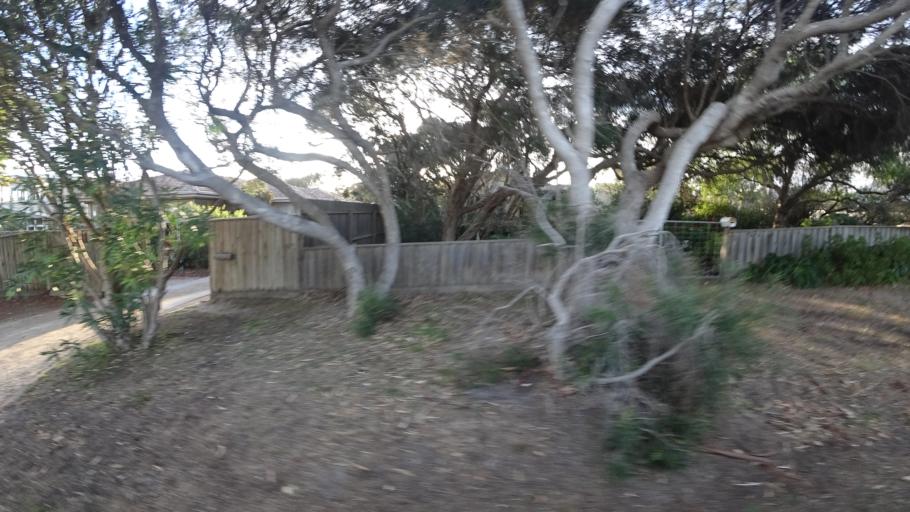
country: AU
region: Victoria
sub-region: Queenscliffe
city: Queenscliff
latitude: -38.2855
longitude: 144.6086
